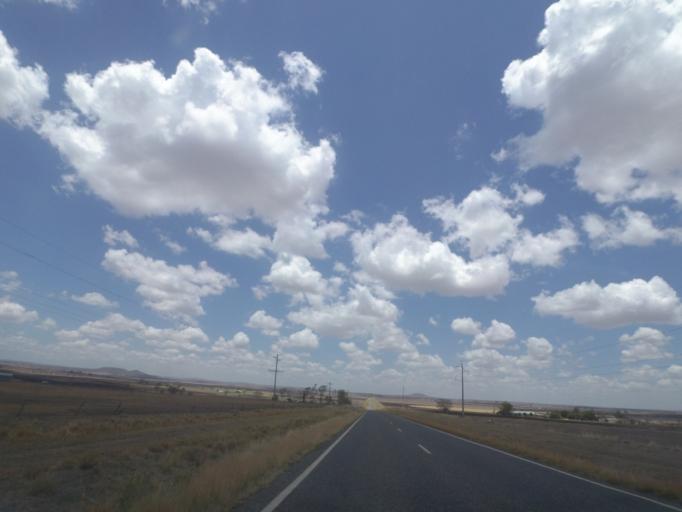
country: AU
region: Queensland
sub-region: Toowoomba
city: Top Camp
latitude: -27.8895
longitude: 151.9726
